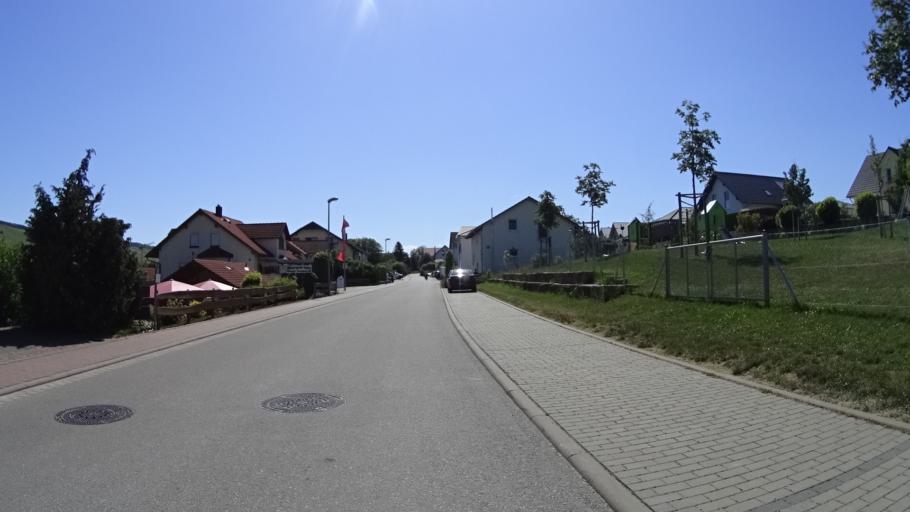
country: DE
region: Baden-Wuerttemberg
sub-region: Regierungsbezirk Stuttgart
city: Igersheim
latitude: 49.4764
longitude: 9.8262
